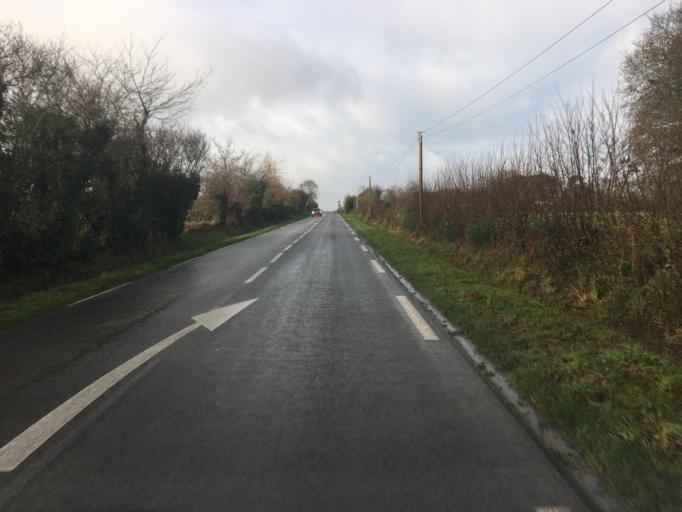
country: FR
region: Lower Normandy
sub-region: Departement de la Manche
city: Saint-Pierre-Eglise
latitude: 49.6687
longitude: -1.3713
